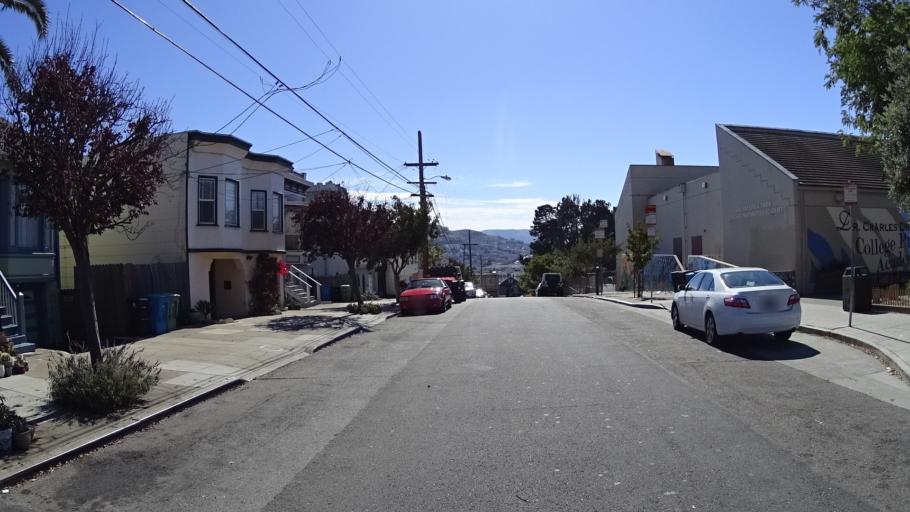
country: US
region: California
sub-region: San Francisco County
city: San Francisco
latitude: 37.7320
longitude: -122.3934
